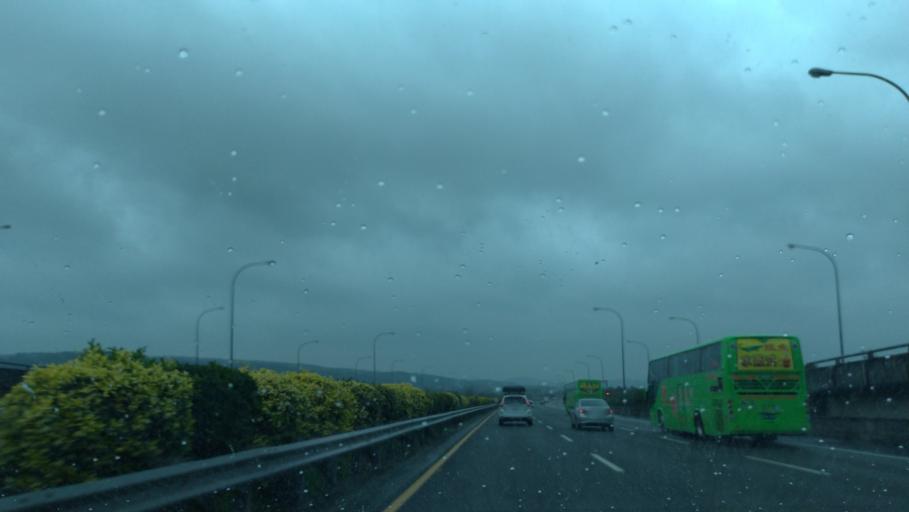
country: TW
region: Taiwan
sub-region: Miaoli
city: Miaoli
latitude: 24.4782
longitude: 120.7843
